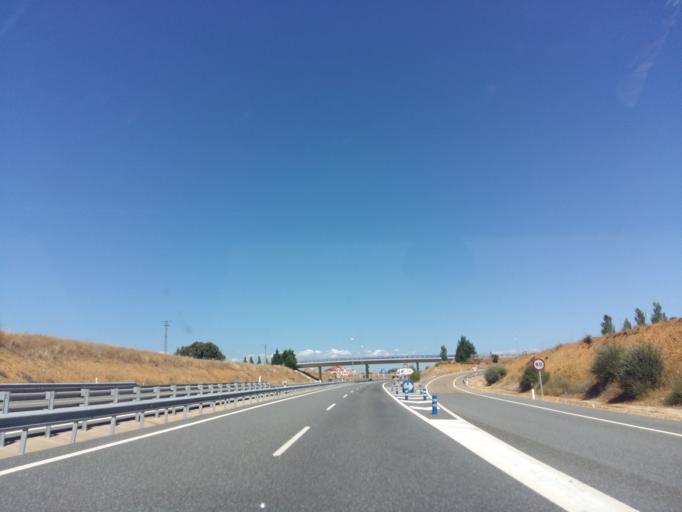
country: ES
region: Castille and Leon
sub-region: Provincia de Leon
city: Villadangos del Paramo
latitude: 42.5223
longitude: -5.7561
